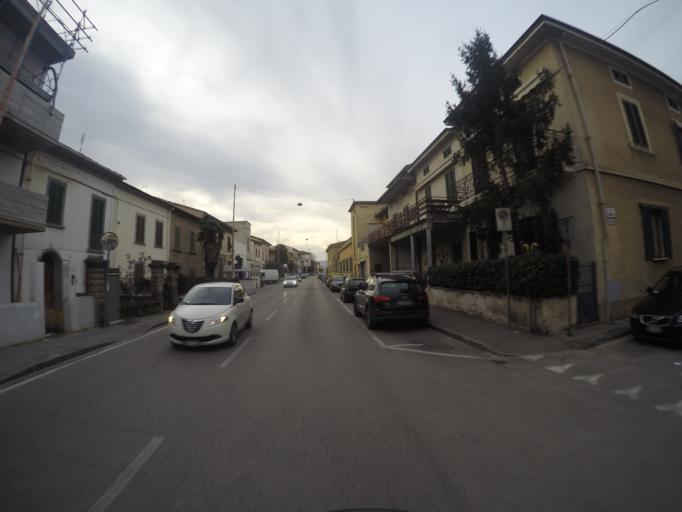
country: IT
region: Tuscany
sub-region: Provincia di Prato
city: Prato
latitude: 43.8760
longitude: 11.0836
